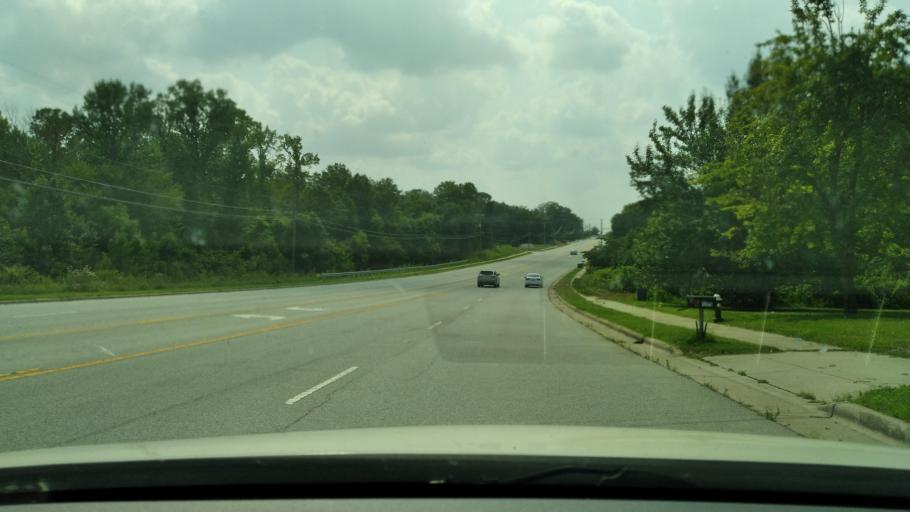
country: US
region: North Carolina
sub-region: Guilford County
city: Jamestown
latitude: 36.0391
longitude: -79.9127
